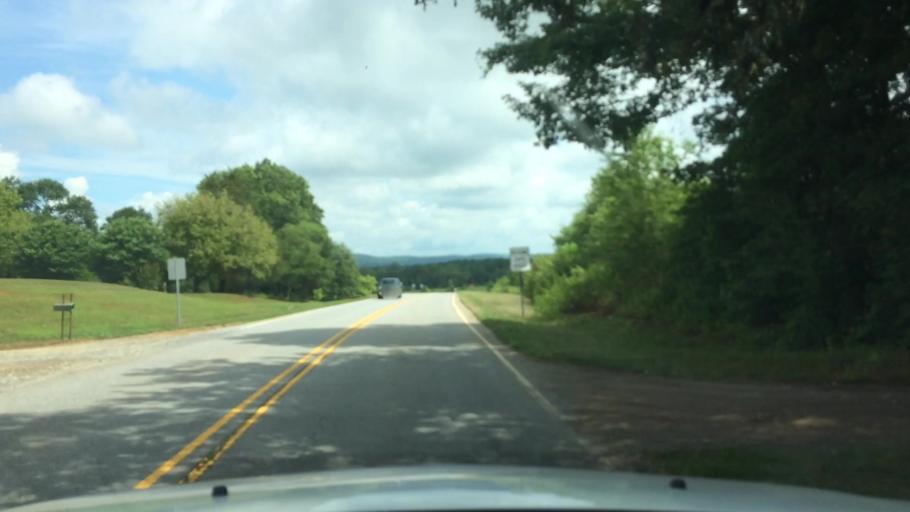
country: US
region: North Carolina
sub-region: Yadkin County
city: Jonesville
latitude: 36.1162
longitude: -80.8572
